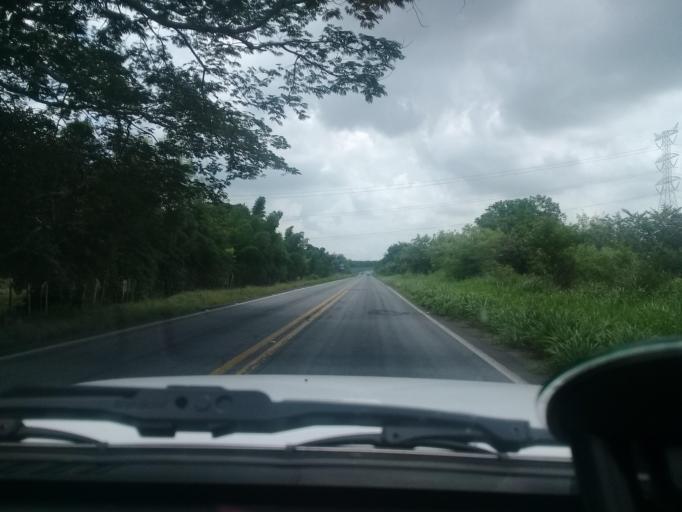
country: MX
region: Veracruz
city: Paso de Ovejas
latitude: 19.2916
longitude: -96.4551
